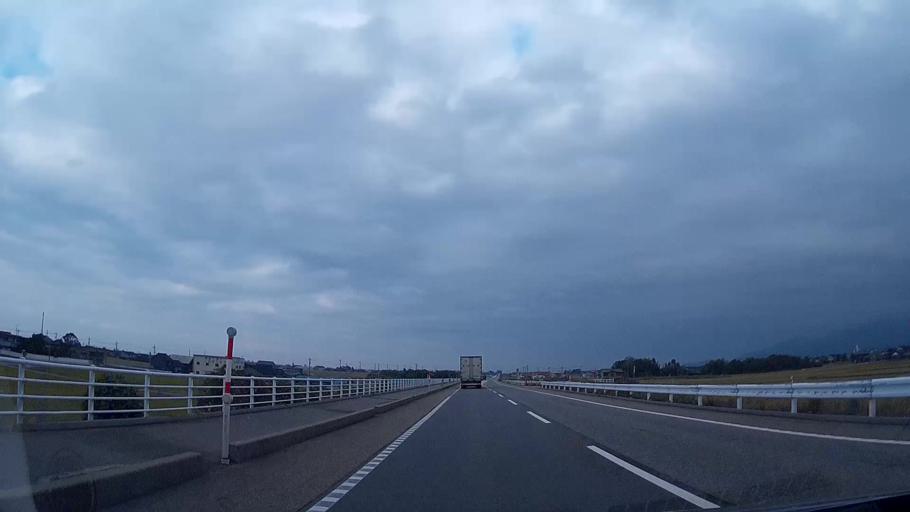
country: JP
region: Toyama
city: Nyuzen
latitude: 36.9099
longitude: 137.4553
